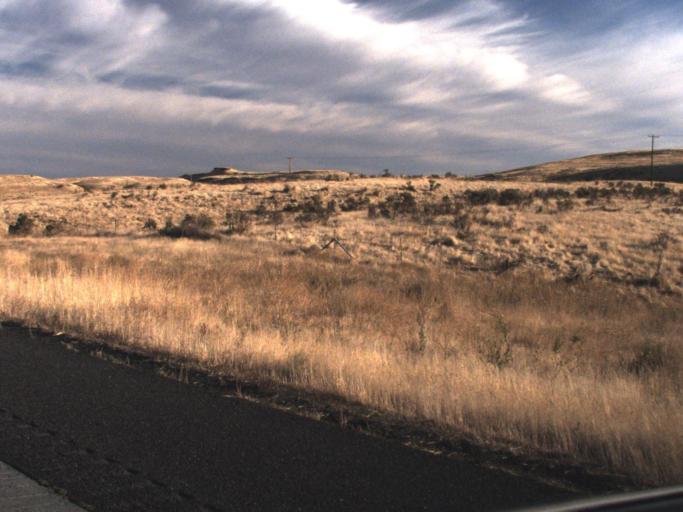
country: US
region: Washington
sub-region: Franklin County
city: Basin City
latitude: 46.4867
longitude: -119.0118
